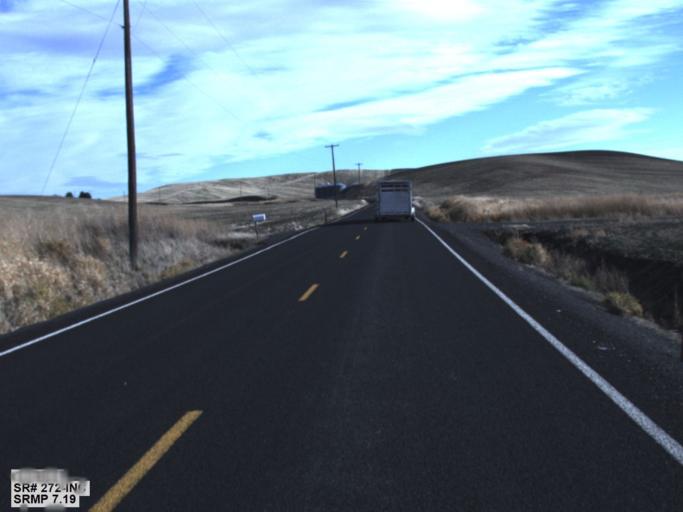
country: US
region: Washington
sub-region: Whitman County
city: Colfax
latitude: 46.9249
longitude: -117.2401
